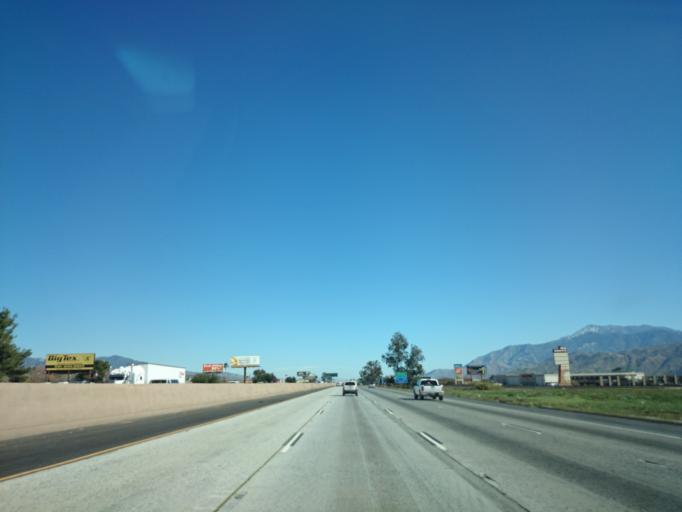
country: US
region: California
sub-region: Riverside County
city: Beaumont
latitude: 33.9271
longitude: -116.9599
